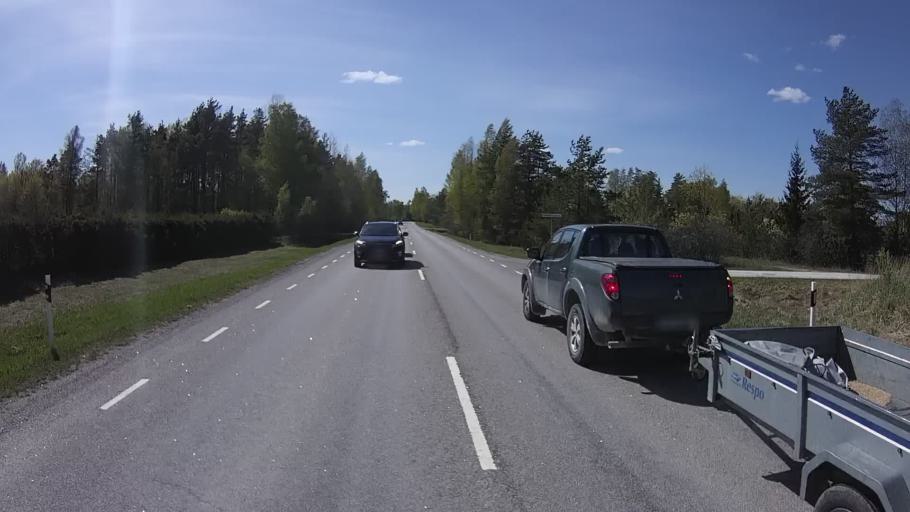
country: EE
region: Laeaene
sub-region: Ridala Parish
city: Uuemoisa
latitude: 58.9628
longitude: 23.6715
